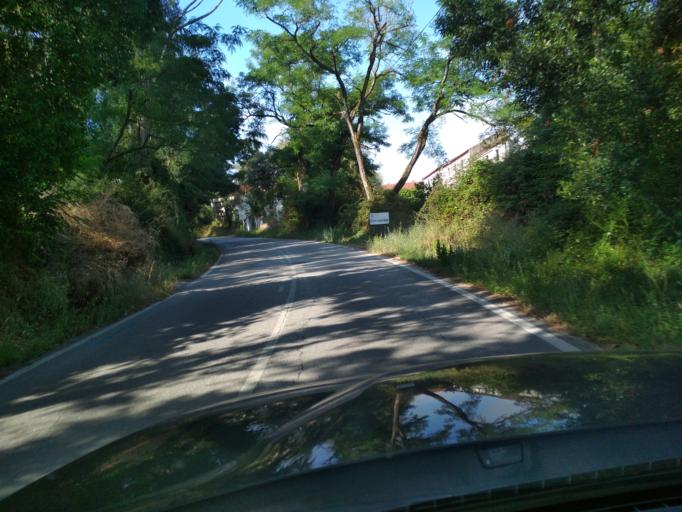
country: PT
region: Coimbra
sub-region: Condeixa-A-Nova
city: Condeixa-a-Nova
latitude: 40.1466
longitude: -8.4673
